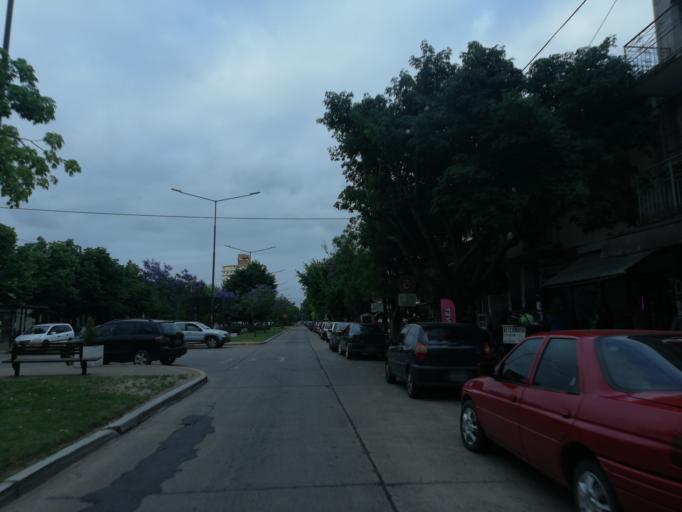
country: AR
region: Buenos Aires
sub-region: Partido de La Plata
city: La Plata
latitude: -34.8528
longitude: -58.0783
